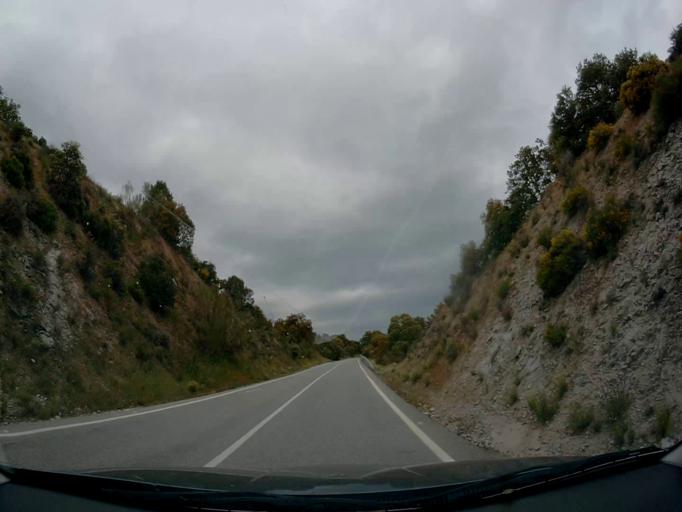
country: ES
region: Madrid
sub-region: Provincia de Madrid
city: Navalagamella
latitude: 40.4310
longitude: -4.1066
